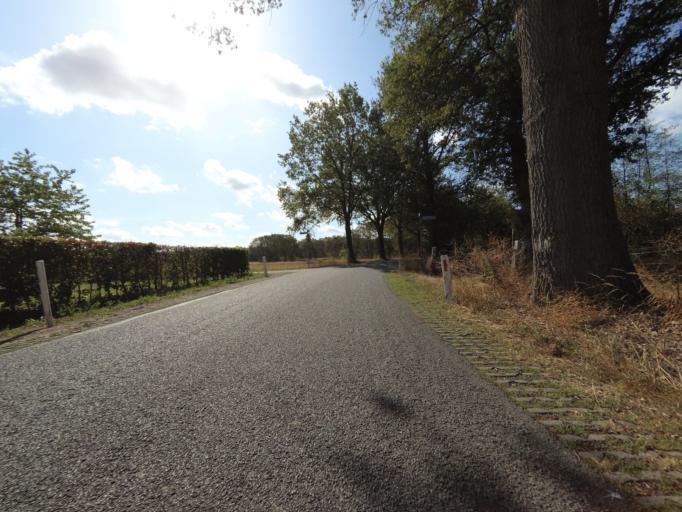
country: NL
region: Overijssel
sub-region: Gemeente Haaksbergen
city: Haaksbergen
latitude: 52.1579
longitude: 6.7623
